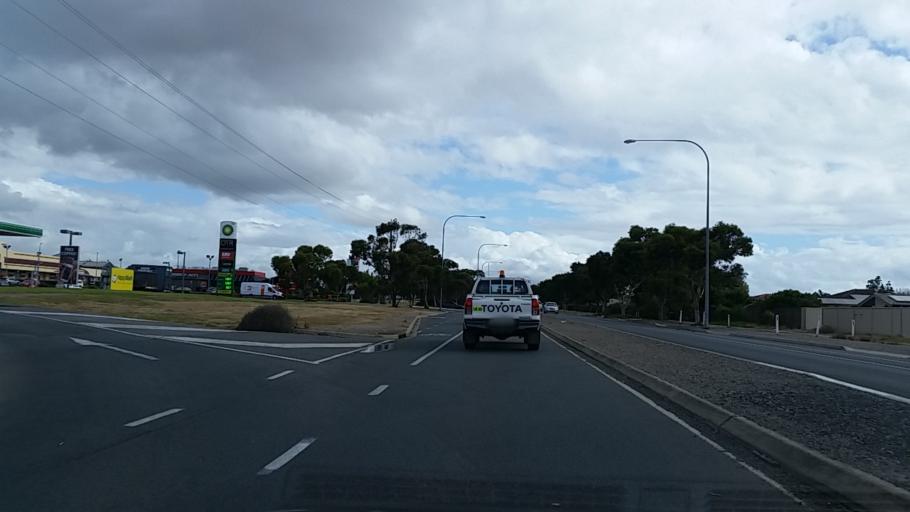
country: AU
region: South Australia
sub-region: Onkaparinga
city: Seaford
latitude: -35.1879
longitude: 138.4773
